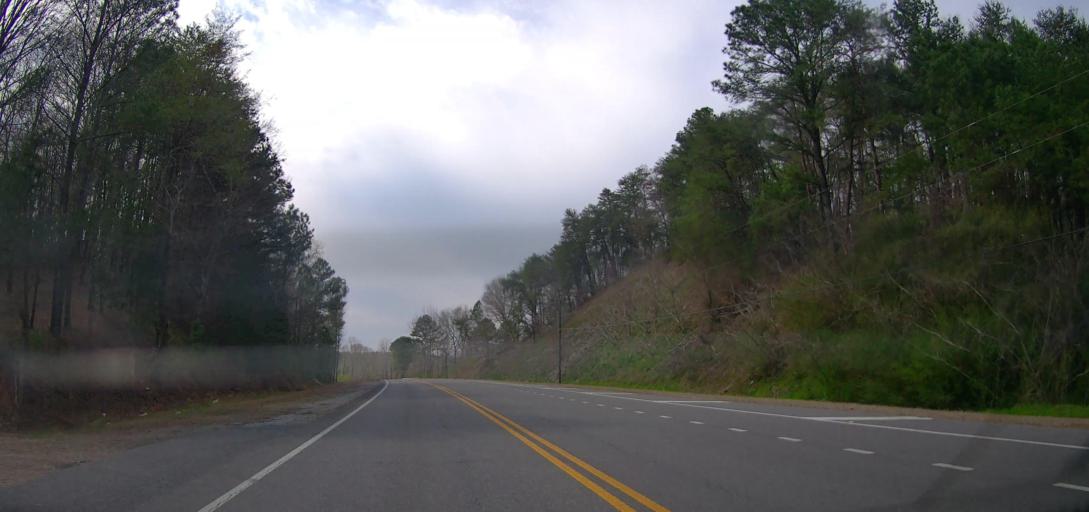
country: US
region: Alabama
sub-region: Walker County
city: Carbon Hill
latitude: 33.9167
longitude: -87.5681
